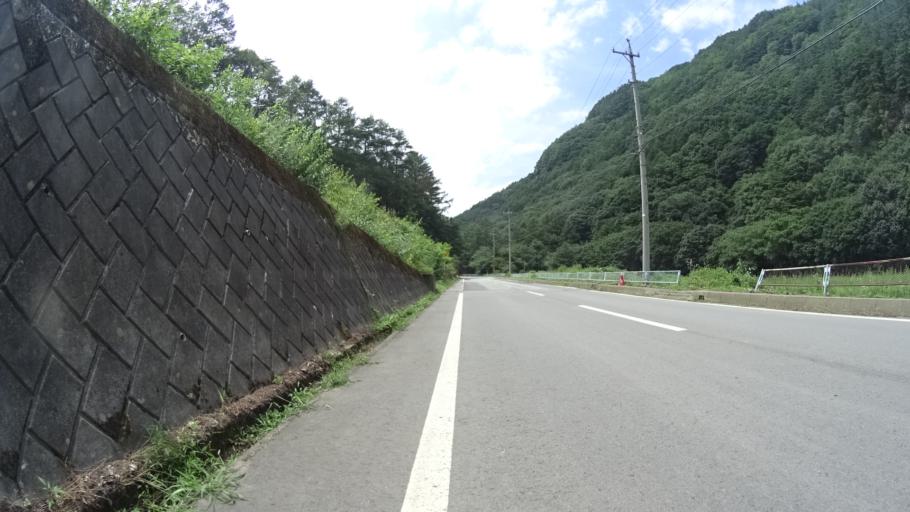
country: JP
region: Nagano
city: Saku
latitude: 36.0604
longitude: 138.5819
